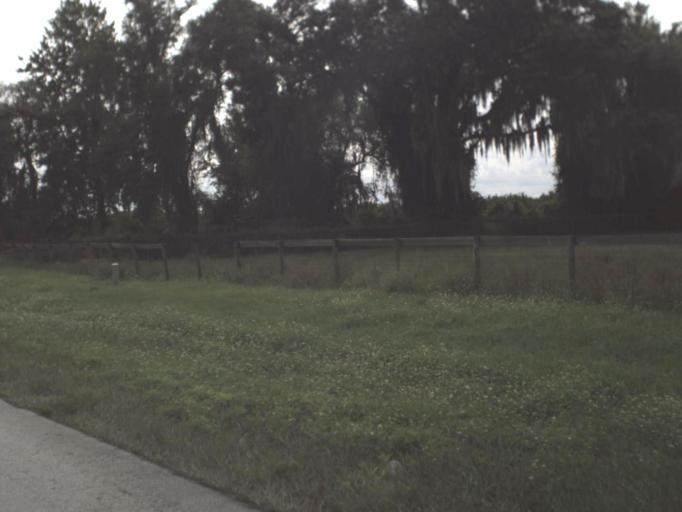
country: US
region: Florida
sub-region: DeSoto County
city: Southeast Arcadia
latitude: 27.2035
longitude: -81.8304
